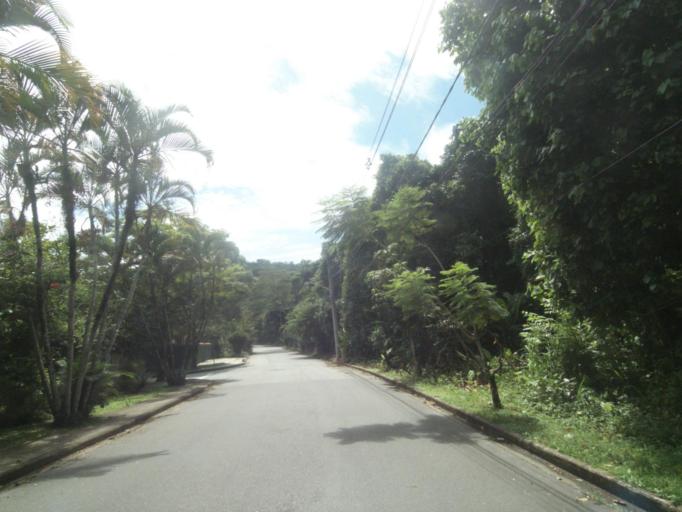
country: BR
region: Rio de Janeiro
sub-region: Niteroi
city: Niteroi
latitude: -22.9539
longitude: -43.0223
